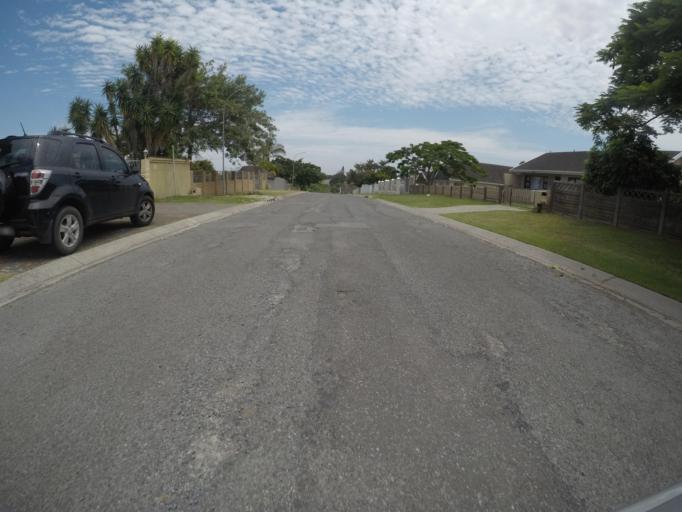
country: ZA
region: Eastern Cape
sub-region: Buffalo City Metropolitan Municipality
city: East London
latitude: -32.9839
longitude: 27.8638
